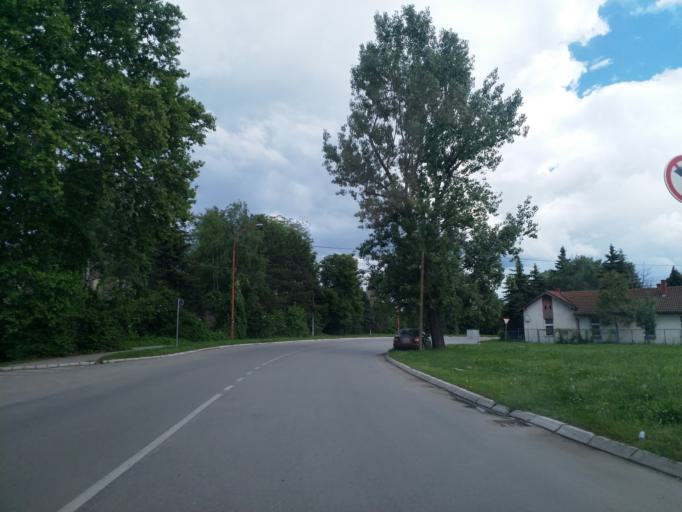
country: RS
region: Central Serbia
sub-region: Pomoravski Okrug
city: Cuprija
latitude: 43.9177
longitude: 21.3760
